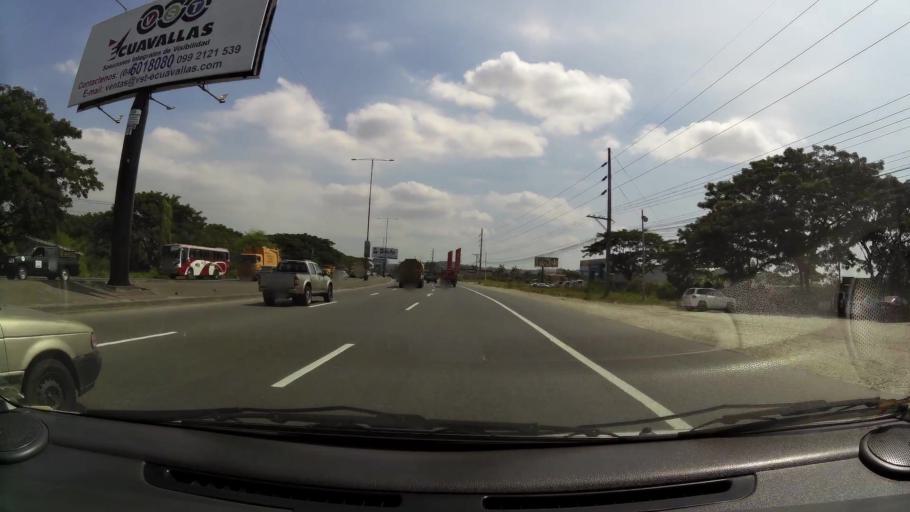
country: EC
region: Guayas
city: Eloy Alfaro
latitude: -2.0505
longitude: -79.8870
